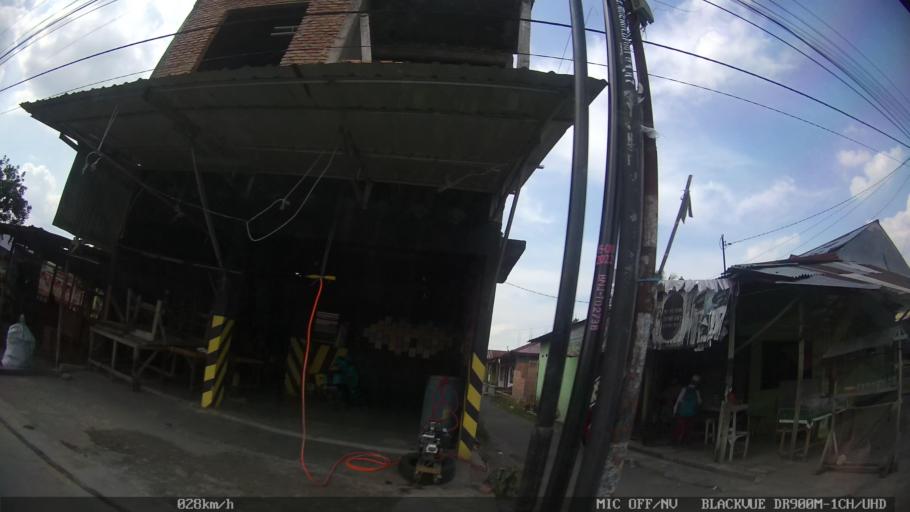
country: ID
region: North Sumatra
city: Binjai
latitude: 3.6133
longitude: 98.5246
